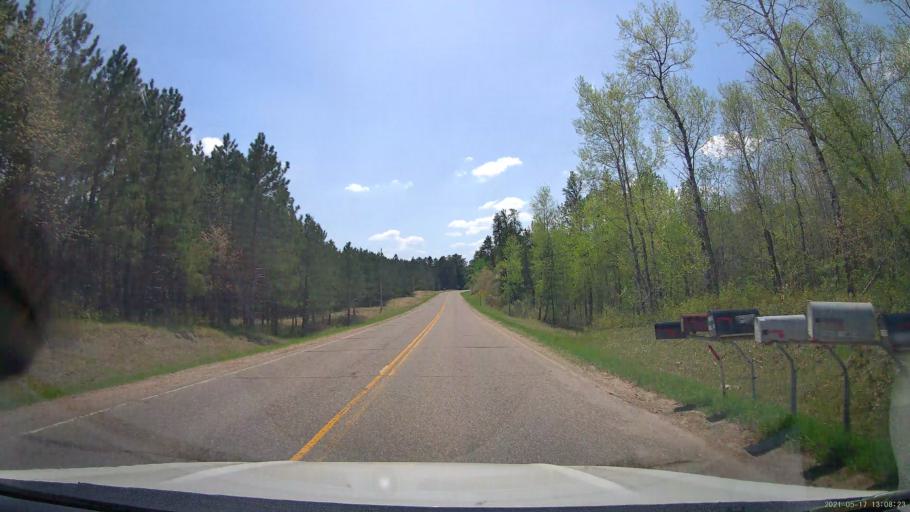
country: US
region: Minnesota
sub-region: Hubbard County
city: Park Rapids
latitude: 47.0384
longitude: -94.9176
